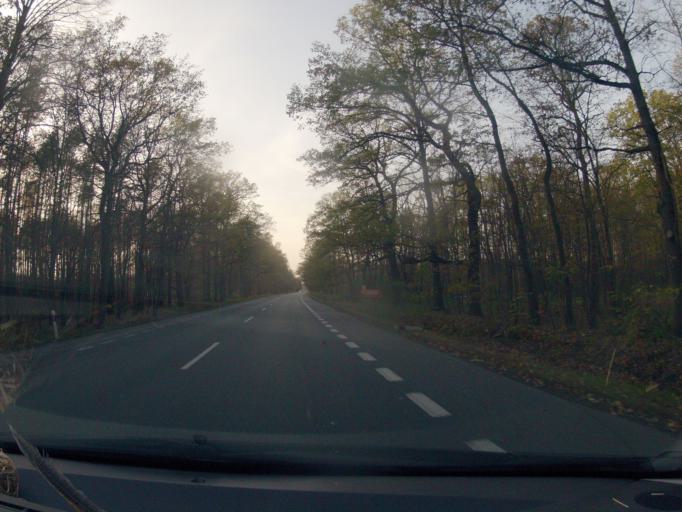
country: PL
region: Opole Voivodeship
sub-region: Powiat opolski
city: Chrzastowice
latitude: 50.6354
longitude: 18.0112
